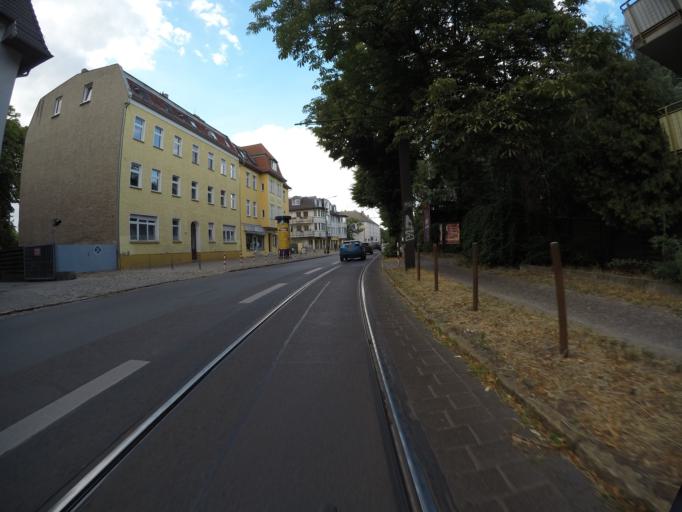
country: DE
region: Berlin
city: Mahlsdorf
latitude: 52.5076
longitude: 13.6127
